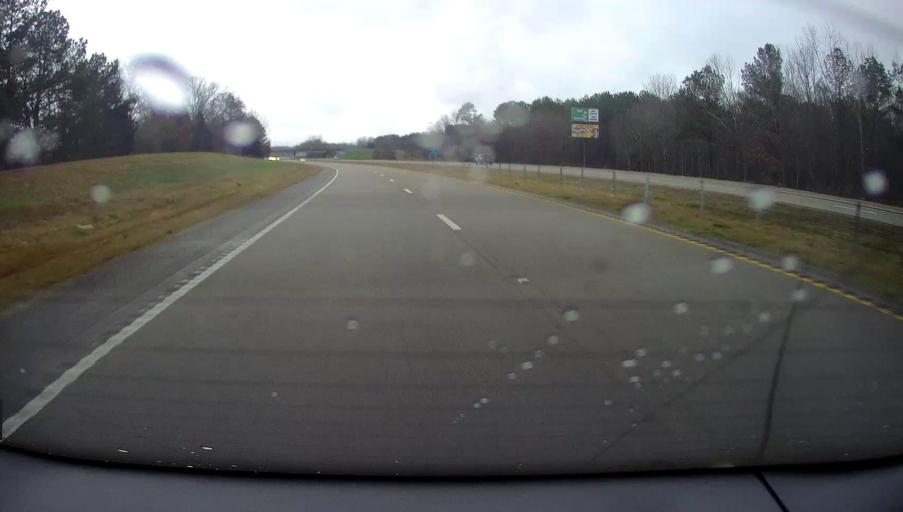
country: US
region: Mississippi
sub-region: Alcorn County
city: Corinth
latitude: 34.9204
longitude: -88.5425
